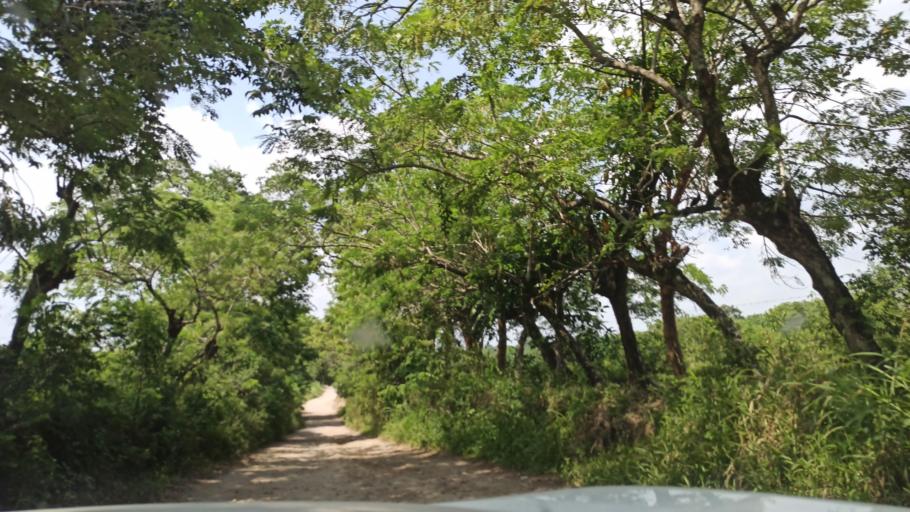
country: MX
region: Veracruz
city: Martinez de la Torre
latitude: 20.0819
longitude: -97.0762
